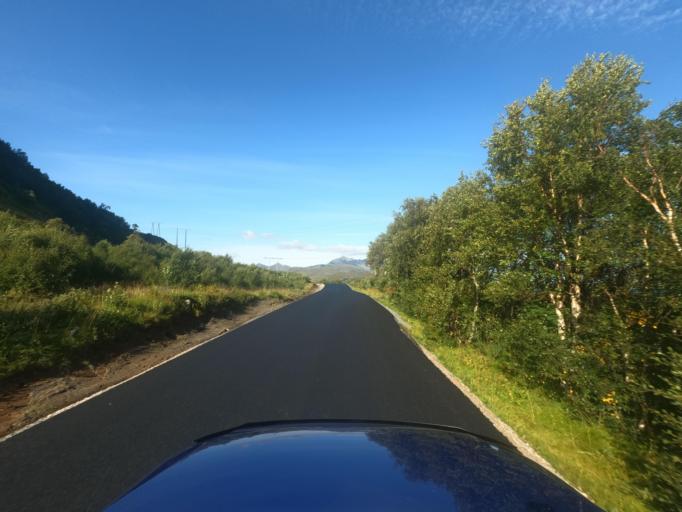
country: NO
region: Nordland
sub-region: Vestvagoy
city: Evjen
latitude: 68.2389
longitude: 13.8270
